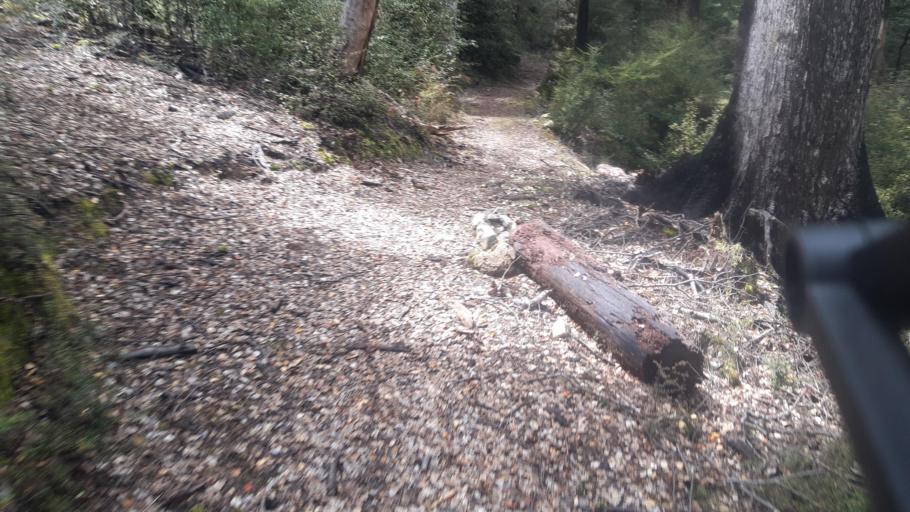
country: NZ
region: Tasman
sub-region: Tasman District
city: Wakefield
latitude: -41.7602
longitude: 172.8040
